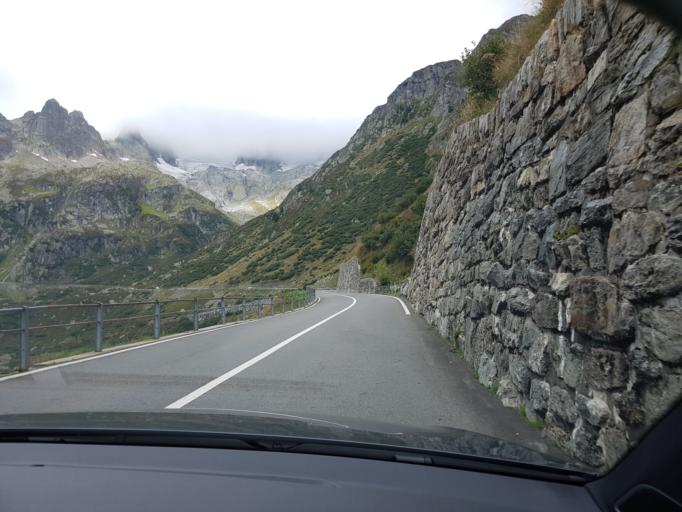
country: CH
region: Obwalden
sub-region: Obwalden
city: Engelberg
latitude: 46.7467
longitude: 8.4782
